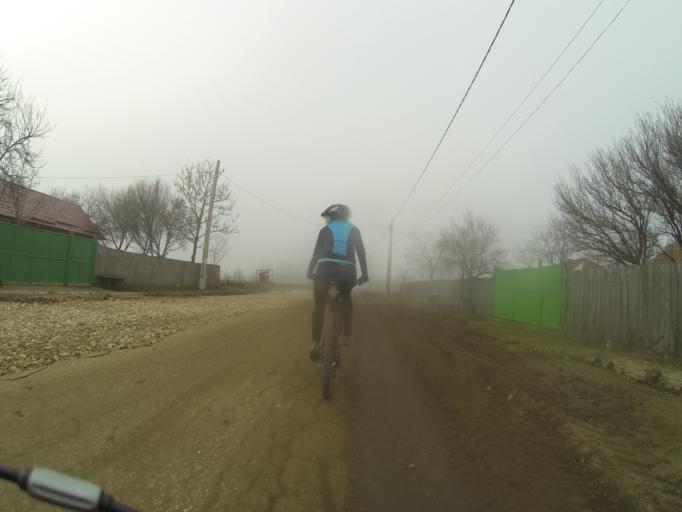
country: RO
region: Mehedinti
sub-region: Comuna Baclesu
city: Baclesu
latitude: 44.4815
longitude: 23.1059
